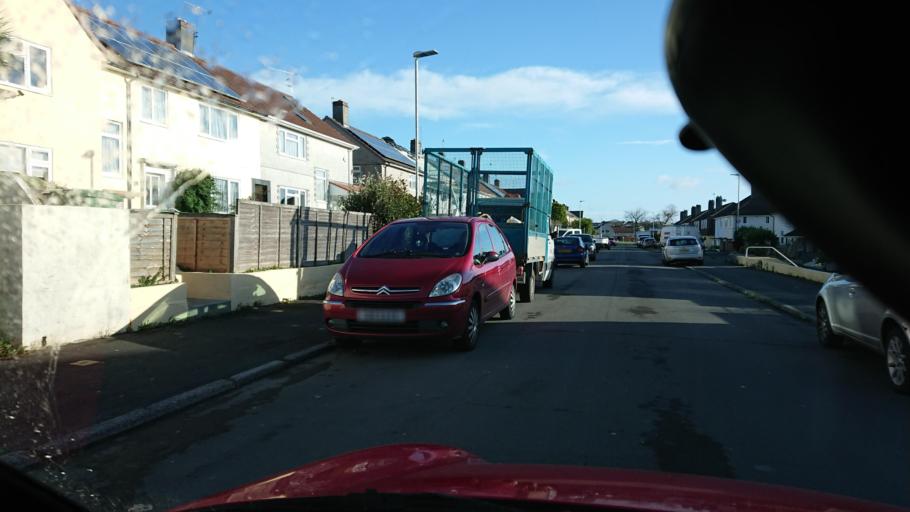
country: GB
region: England
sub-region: Cornwall
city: Torpoint
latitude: 50.4099
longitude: -4.1670
